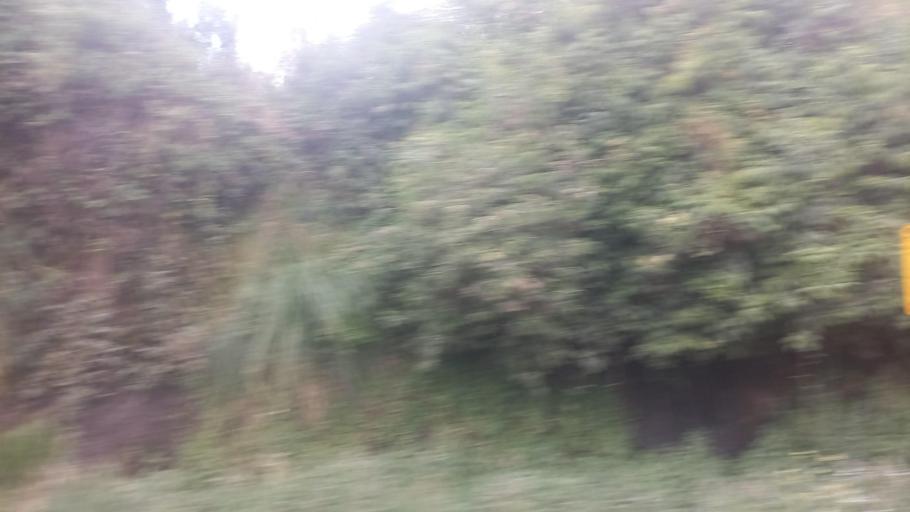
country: EC
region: Pichincha
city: Cayambe
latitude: 0.0732
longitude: -78.1080
